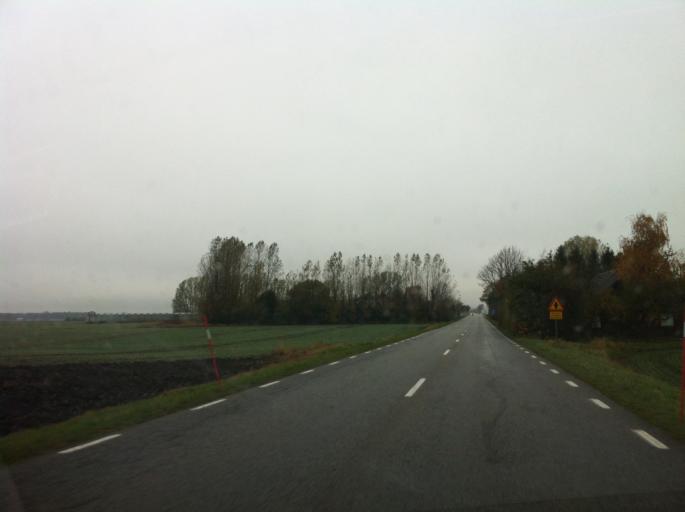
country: SE
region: Skane
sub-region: Landskrona
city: Asmundtorp
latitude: 55.8663
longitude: 12.9929
